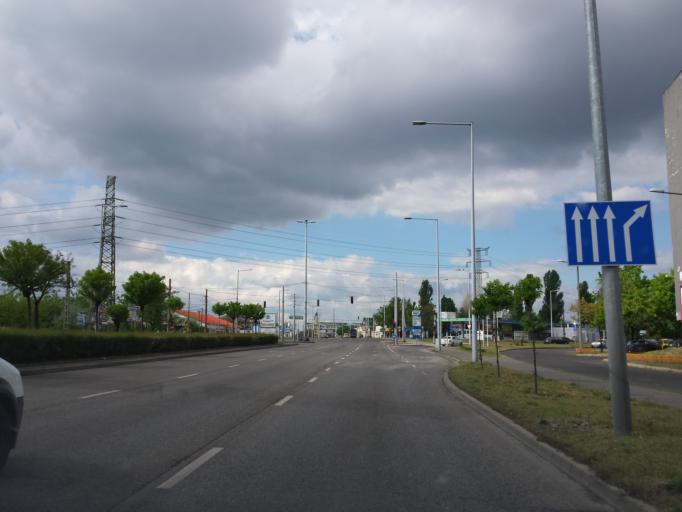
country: HU
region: Budapest
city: Budapest XX. keruelet
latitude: 47.4408
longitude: 19.0939
